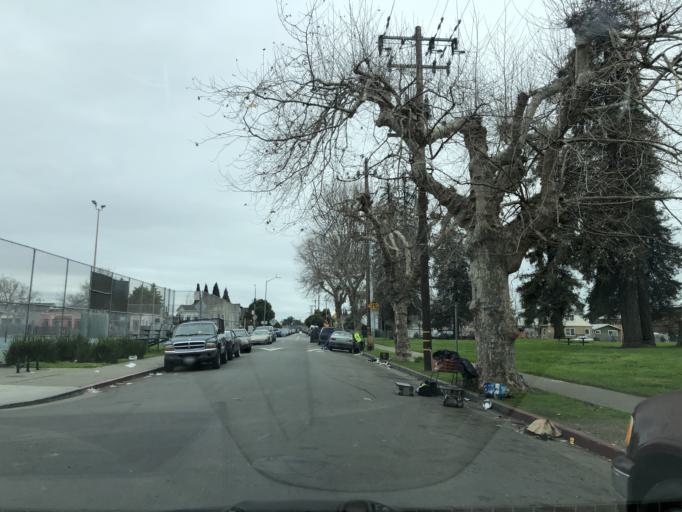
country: US
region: California
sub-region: Alameda County
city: San Leandro
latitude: 37.7435
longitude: -122.1745
